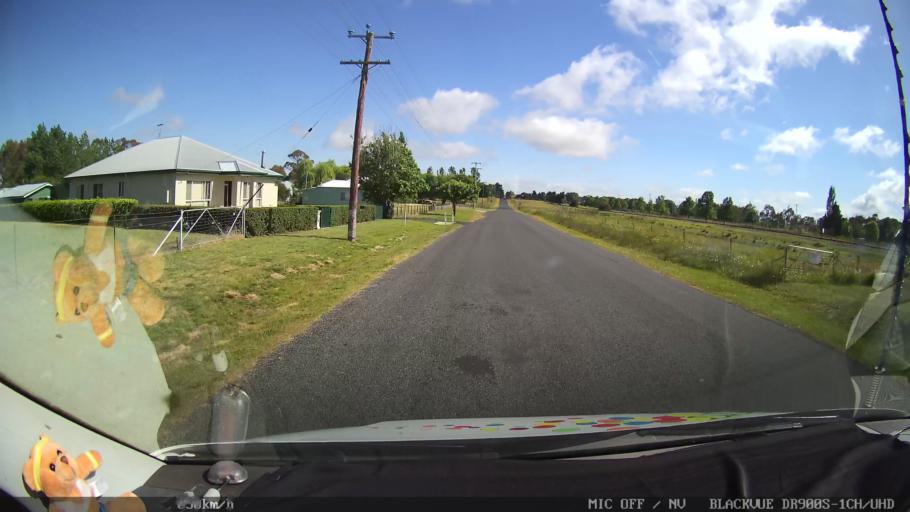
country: AU
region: New South Wales
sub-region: Guyra
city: Guyra
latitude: -30.2113
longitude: 151.6733
